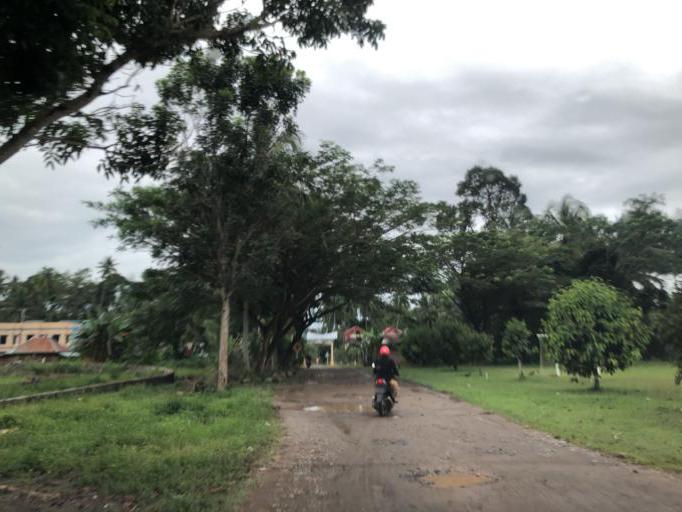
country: ID
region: West Sumatra
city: Pauhambar
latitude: -0.6191
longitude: 100.2132
